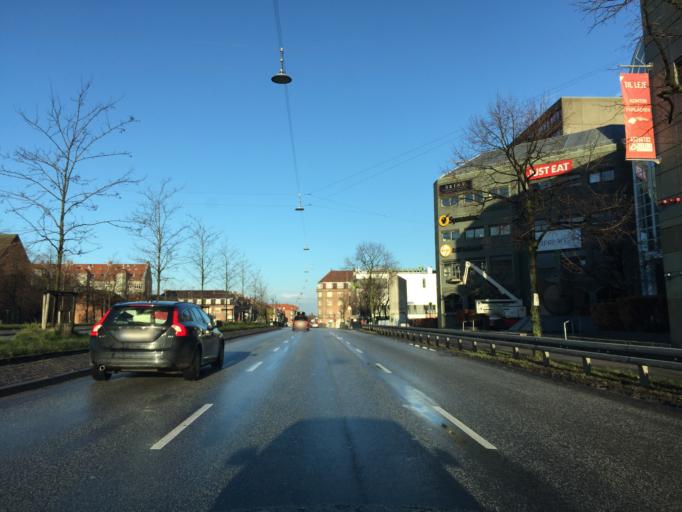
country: DK
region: Capital Region
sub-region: Kobenhavn
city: Copenhagen
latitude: 55.7083
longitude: 12.5622
